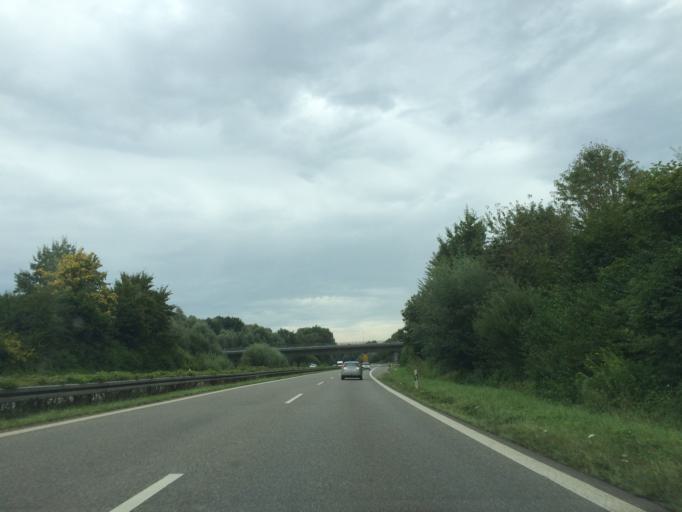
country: DE
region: Baden-Wuerttemberg
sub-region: Tuebingen Region
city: Berg
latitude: 47.8179
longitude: 9.6102
